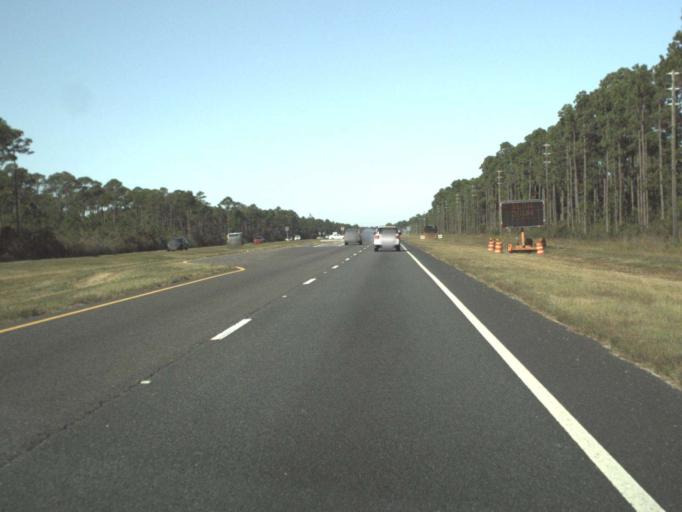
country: US
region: Florida
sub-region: Walton County
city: Seaside
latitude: 30.3680
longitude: -86.1893
